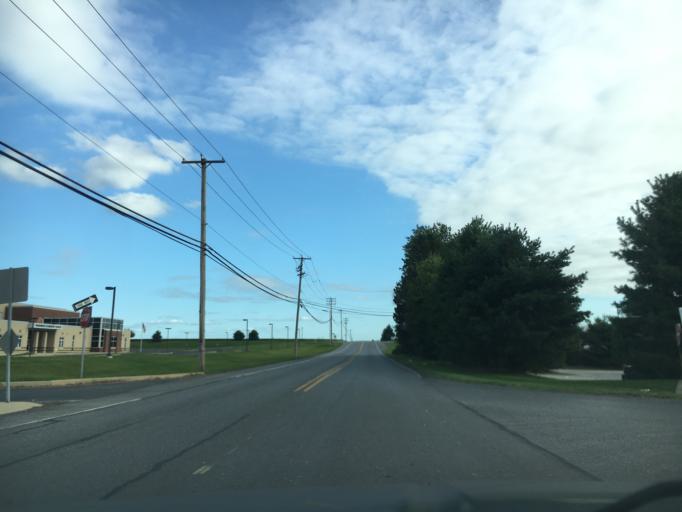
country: US
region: Pennsylvania
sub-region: Berks County
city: Topton
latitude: 40.5909
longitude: -75.7109
